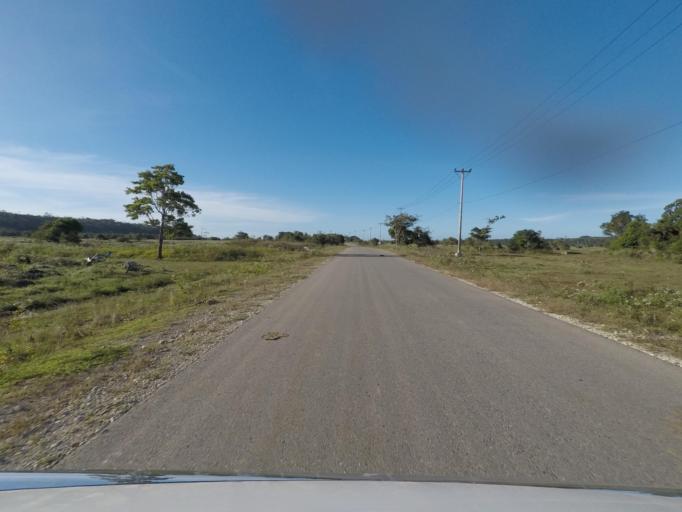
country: TL
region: Lautem
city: Lospalos
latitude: -8.3954
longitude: 127.0084
